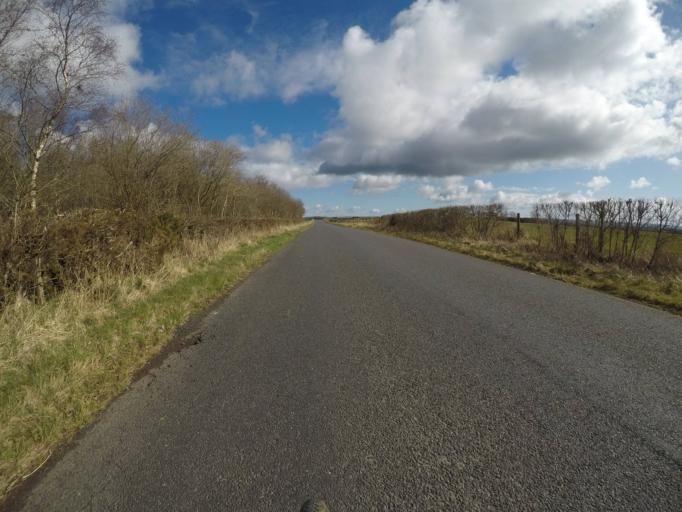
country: GB
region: Scotland
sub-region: North Ayrshire
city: Kilwinning
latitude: 55.6817
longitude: -4.6519
